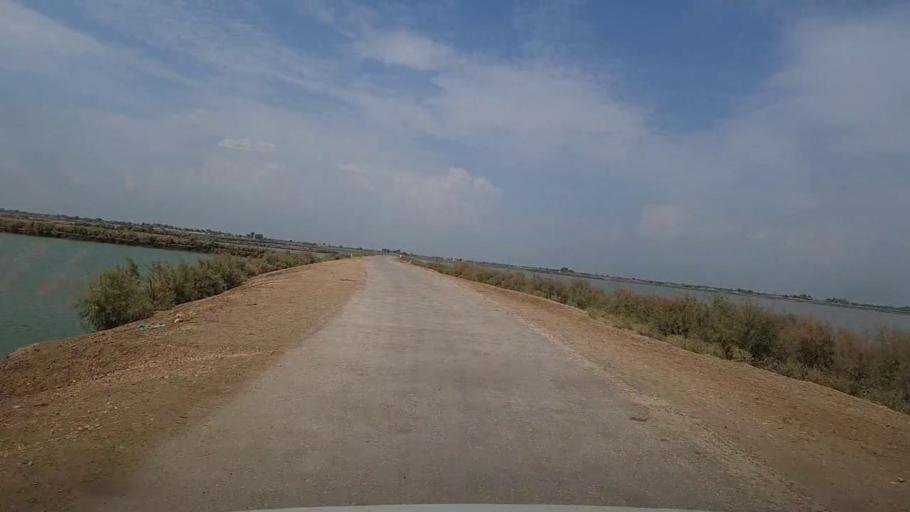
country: PK
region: Sindh
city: Thul
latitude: 28.2779
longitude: 68.8216
